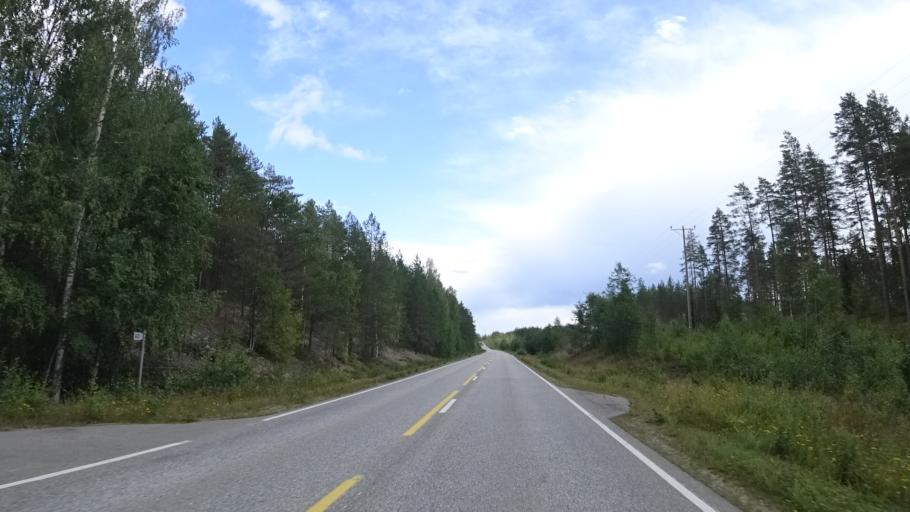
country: FI
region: North Karelia
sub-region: Joensuu
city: Ilomantsi
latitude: 62.6436
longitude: 31.0422
